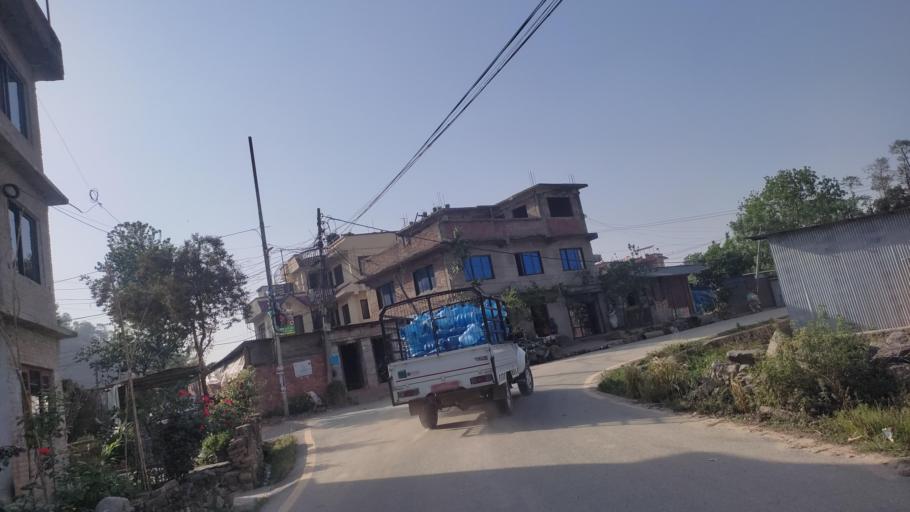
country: NP
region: Central Region
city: Kirtipur
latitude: 27.6521
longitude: 85.2761
